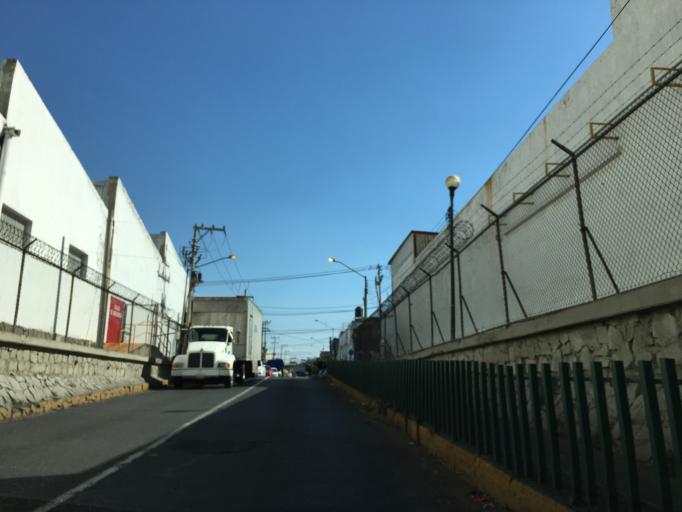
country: MX
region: Jalisco
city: Guadalajara
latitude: 20.6611
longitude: -103.3674
